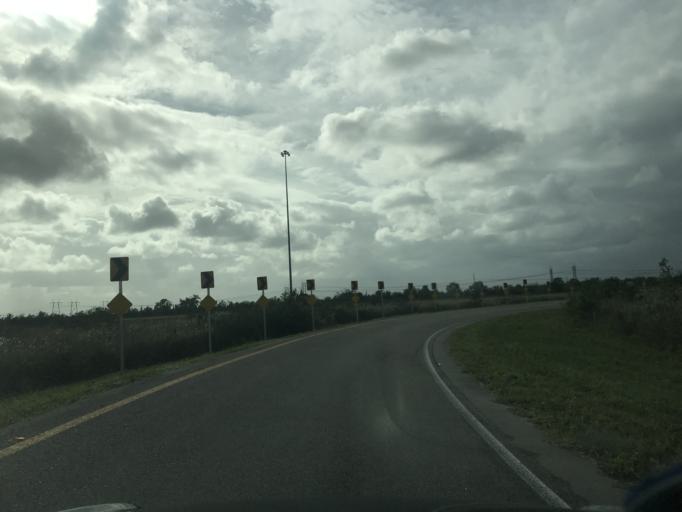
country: US
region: Florida
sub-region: Broward County
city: Weston
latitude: 26.1421
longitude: -80.4397
